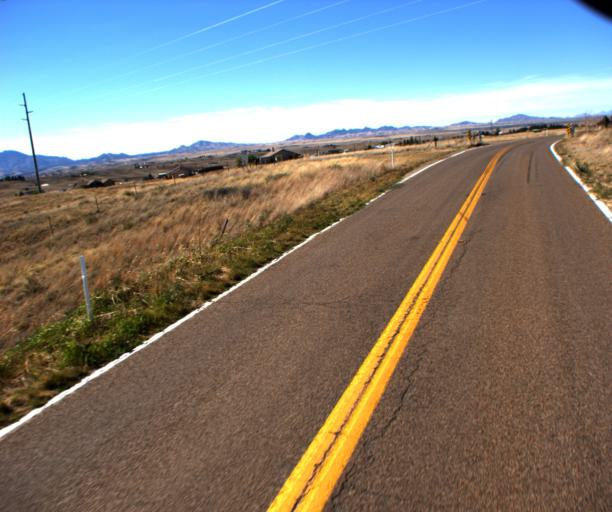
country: US
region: Arizona
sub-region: Cochise County
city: Huachuca City
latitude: 31.6529
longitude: -110.6046
